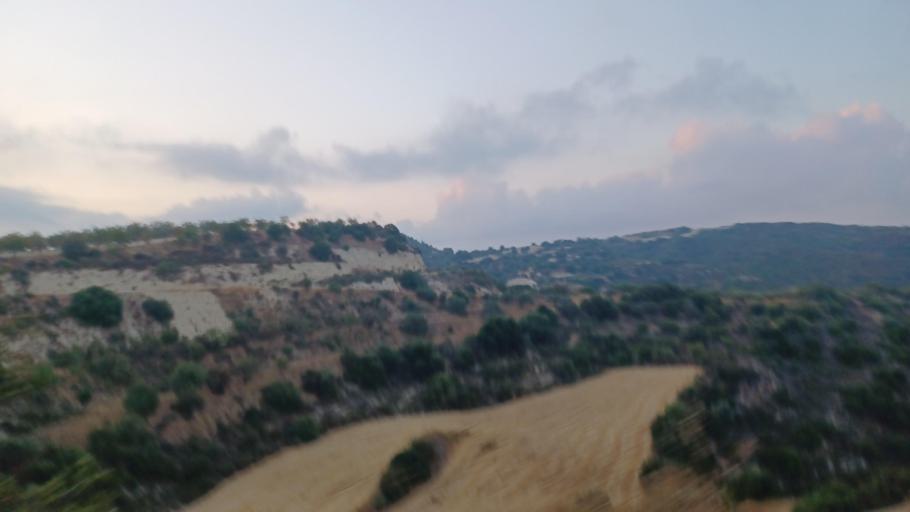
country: CY
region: Pafos
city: Mesogi
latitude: 34.8099
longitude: 32.5762
